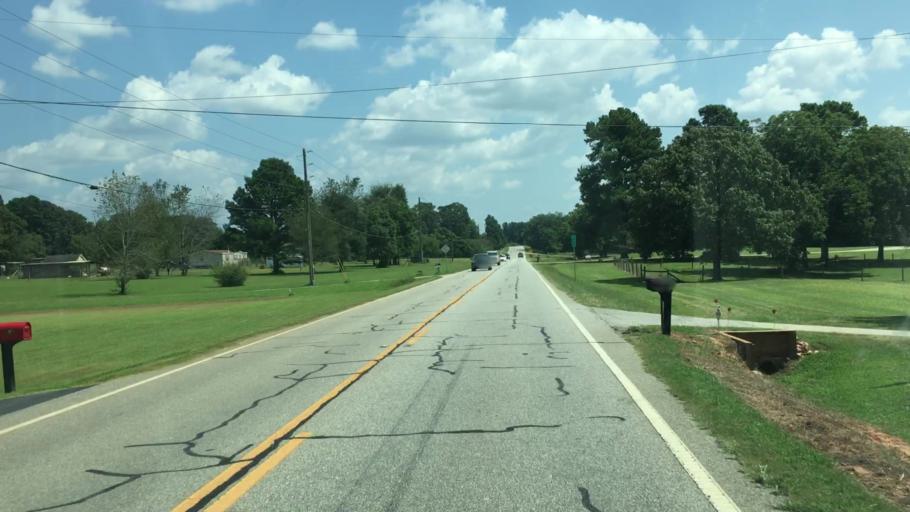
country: US
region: Georgia
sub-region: Barrow County
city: Statham
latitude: 33.9414
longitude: -83.6410
